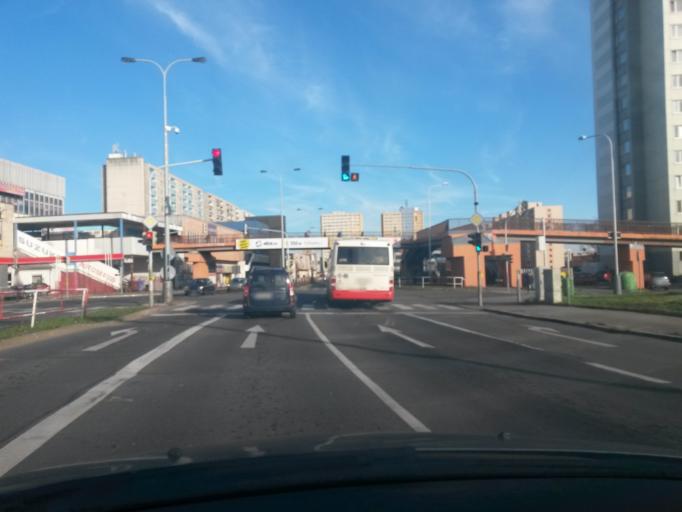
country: CZ
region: Central Bohemia
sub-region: Okres Praha-Zapad
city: Pruhonice
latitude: 50.0304
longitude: 14.5279
